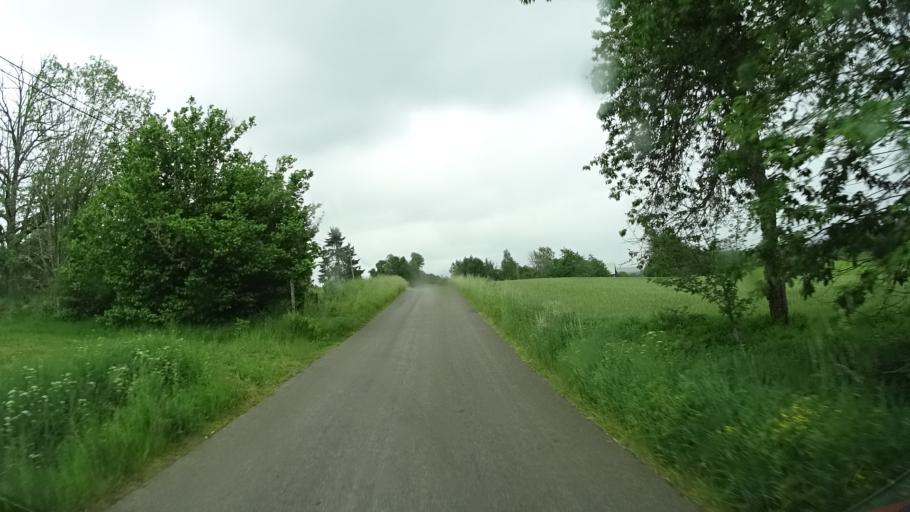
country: SE
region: Joenkoeping
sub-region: Eksjo Kommun
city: Mariannelund
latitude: 57.6829
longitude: 15.5750
